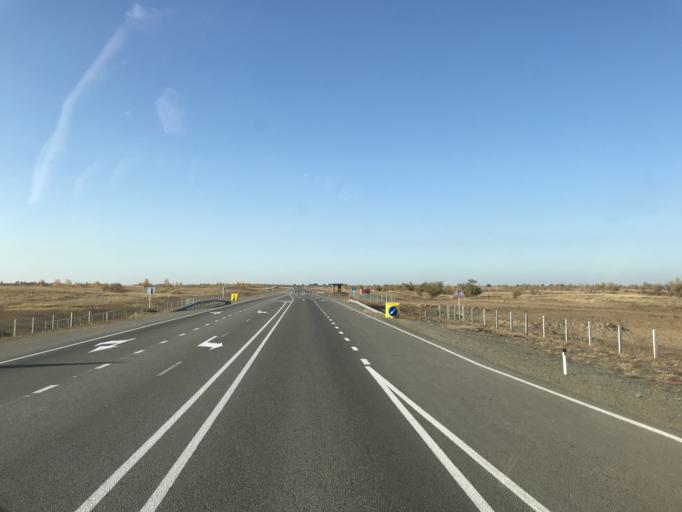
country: KZ
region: Pavlodar
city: Koktobe
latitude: 51.8145
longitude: 77.4710
